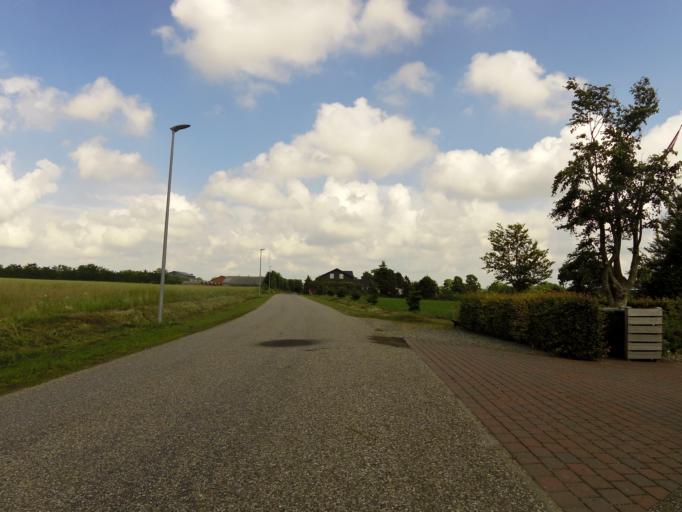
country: DK
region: South Denmark
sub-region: Vejen Kommune
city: Rodding
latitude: 55.3302
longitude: 9.0502
